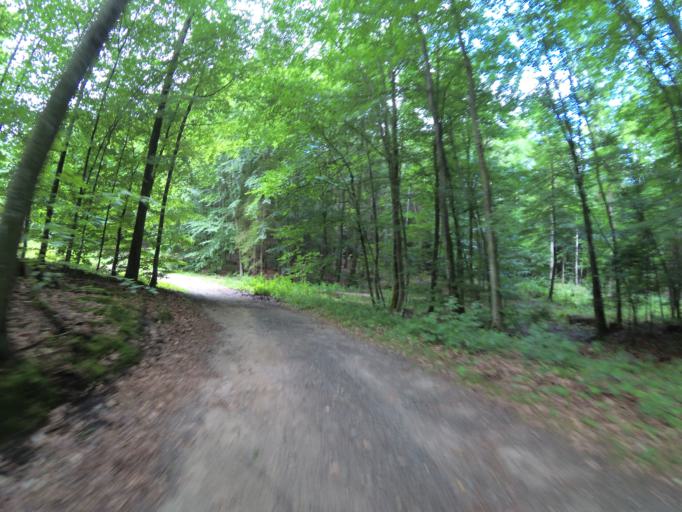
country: PL
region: Pomeranian Voivodeship
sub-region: Gdynia
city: Wielki Kack
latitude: 54.5108
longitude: 18.4458
